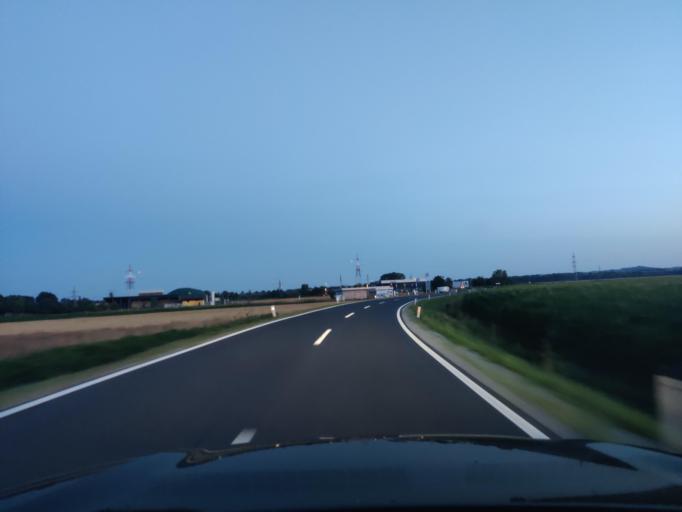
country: SI
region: Lendava-Lendva
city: Lendava
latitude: 46.5449
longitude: 16.4436
